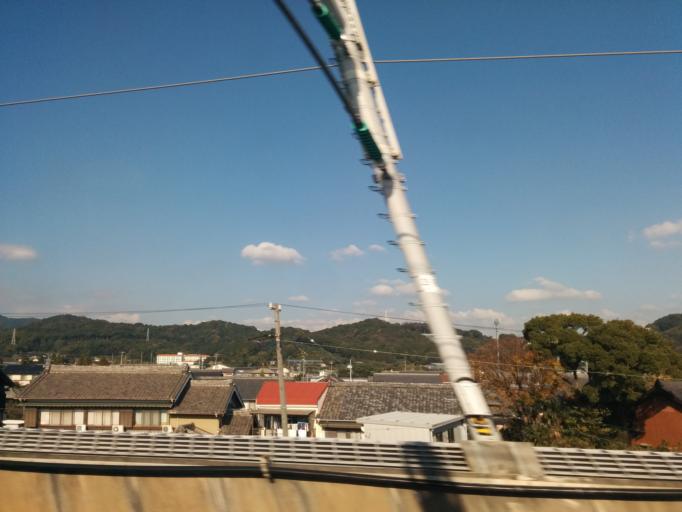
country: JP
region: Aichi
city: Kozakai-cho
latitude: 34.8119
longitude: 137.3020
